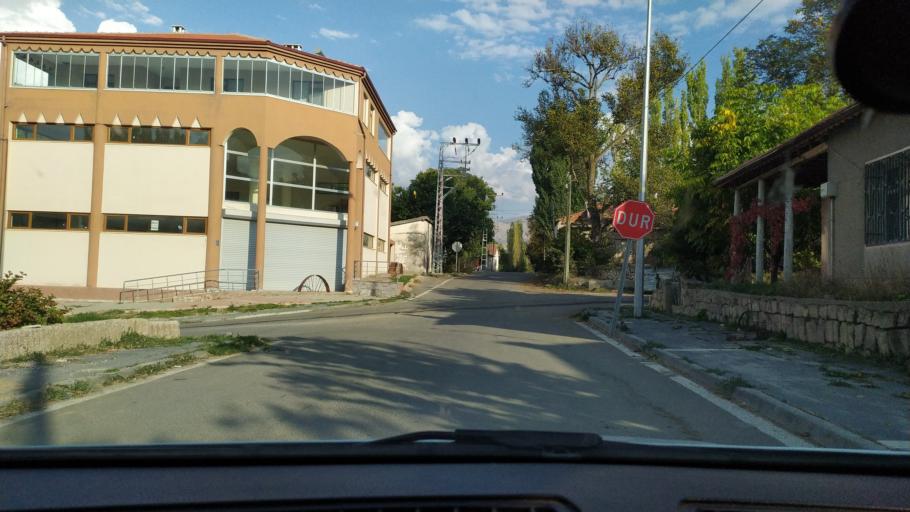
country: TR
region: Kayseri
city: Akkisla
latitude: 38.9996
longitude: 36.1696
